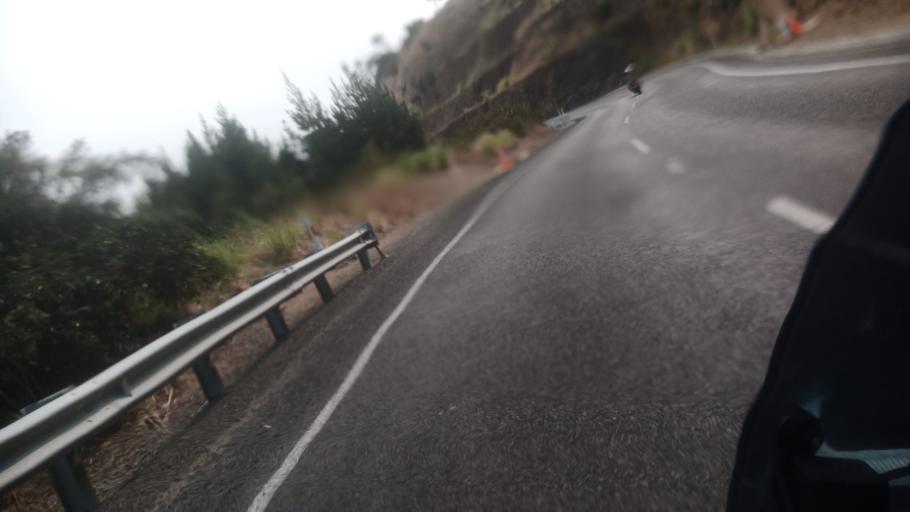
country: NZ
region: Bay of Plenty
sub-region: Opotiki District
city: Opotiki
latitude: -37.8907
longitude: 177.5558
